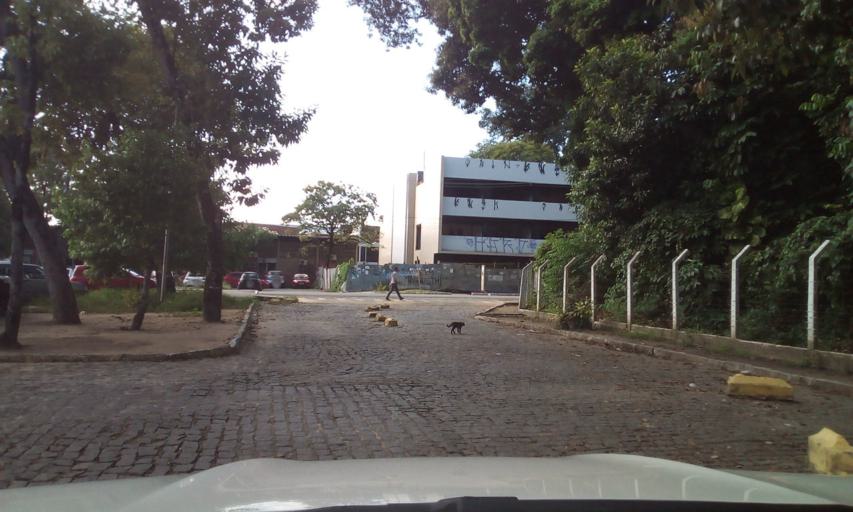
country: BR
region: Paraiba
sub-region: Joao Pessoa
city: Joao Pessoa
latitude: -7.1390
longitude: -34.8493
